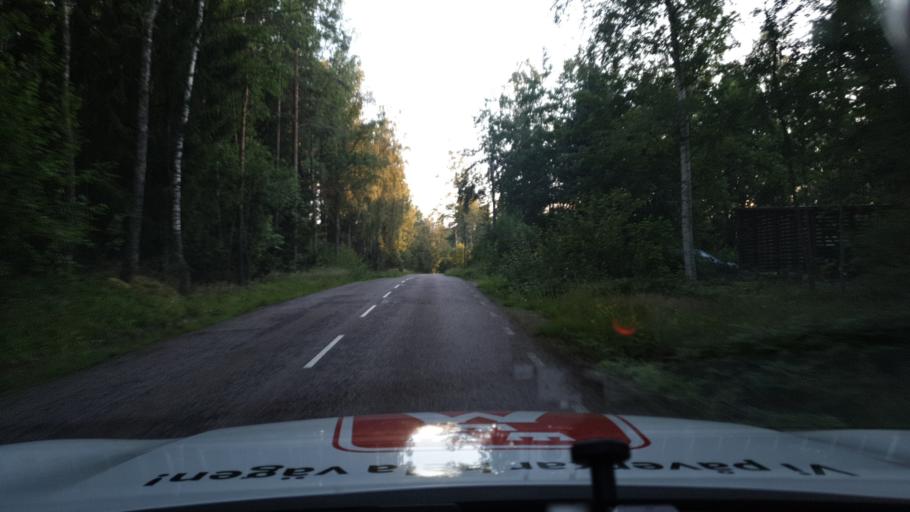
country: SE
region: Dalarna
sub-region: Avesta Kommun
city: Horndal
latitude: 60.1701
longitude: 16.4881
